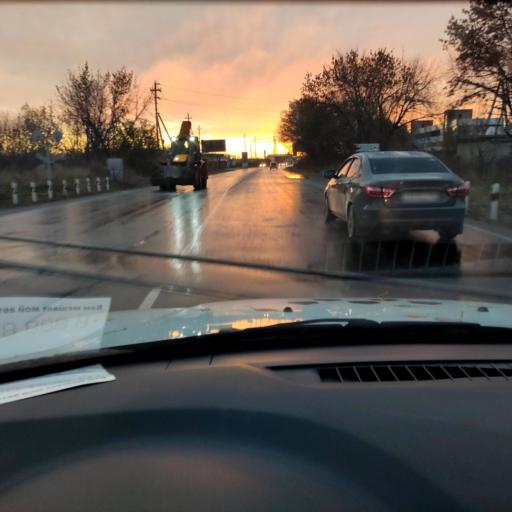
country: RU
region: Samara
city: Tol'yatti
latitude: 53.5298
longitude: 49.4681
